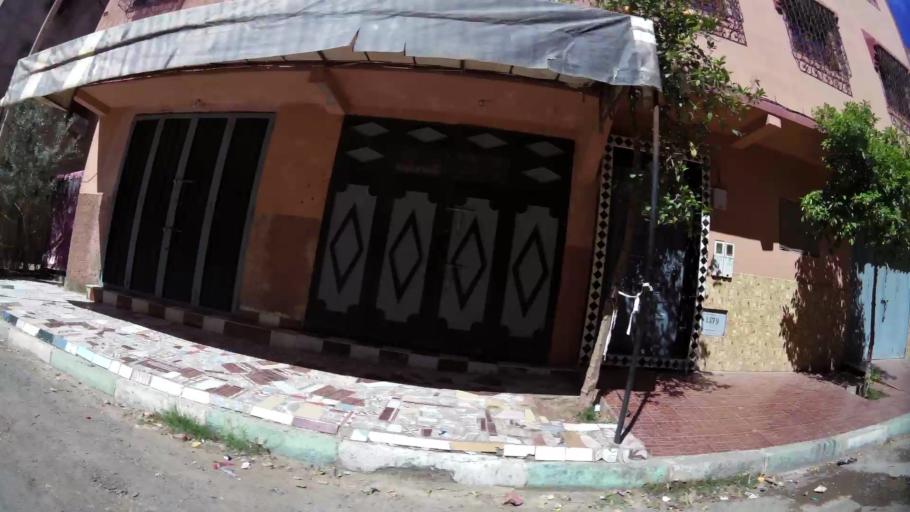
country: MA
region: Marrakech-Tensift-Al Haouz
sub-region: Marrakech
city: Marrakesh
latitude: 31.6431
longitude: -8.1154
